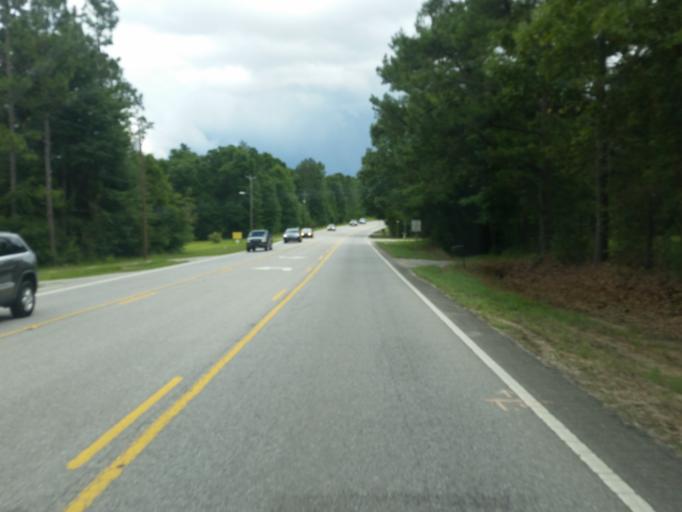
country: US
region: Mississippi
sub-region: George County
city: Lucedale
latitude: 30.8507
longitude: -88.4021
